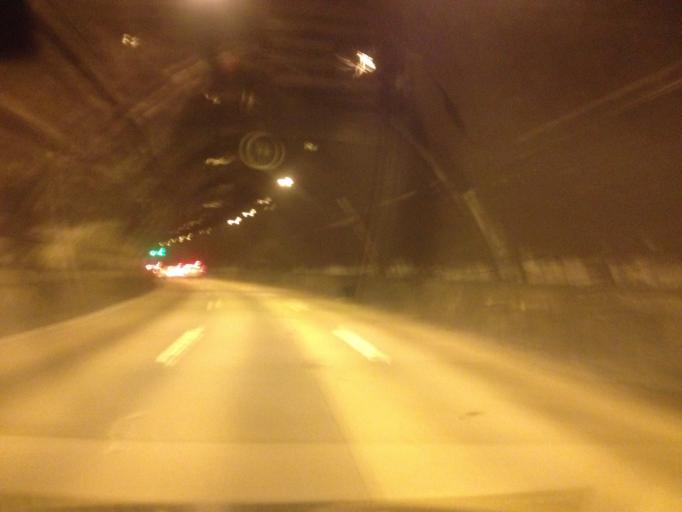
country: BR
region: Rio de Janeiro
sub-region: Rio De Janeiro
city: Rio de Janeiro
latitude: -22.9382
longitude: -43.2033
